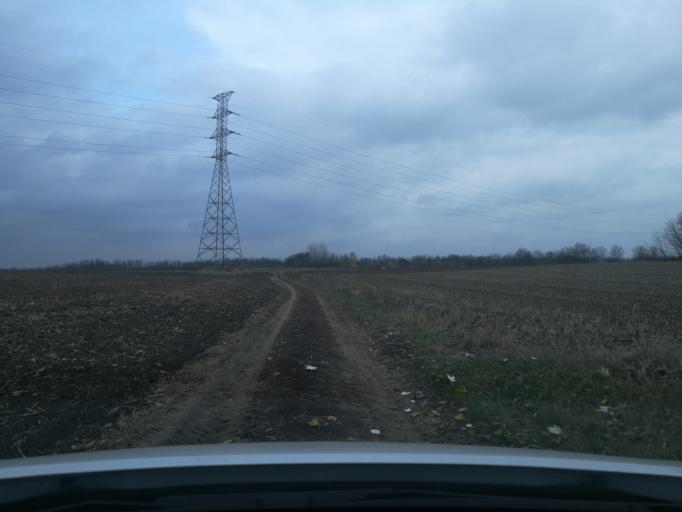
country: HU
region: Szabolcs-Szatmar-Bereg
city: Nyirpazony
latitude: 47.9653
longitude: 21.7844
